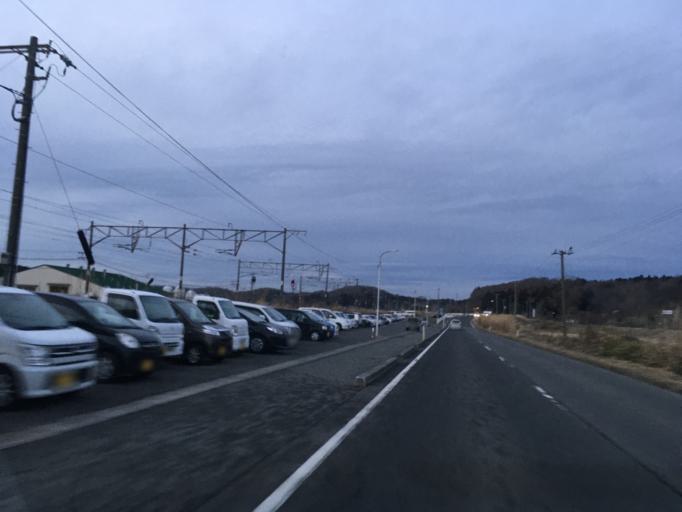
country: JP
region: Miyagi
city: Kogota
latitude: 38.6573
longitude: 141.0739
